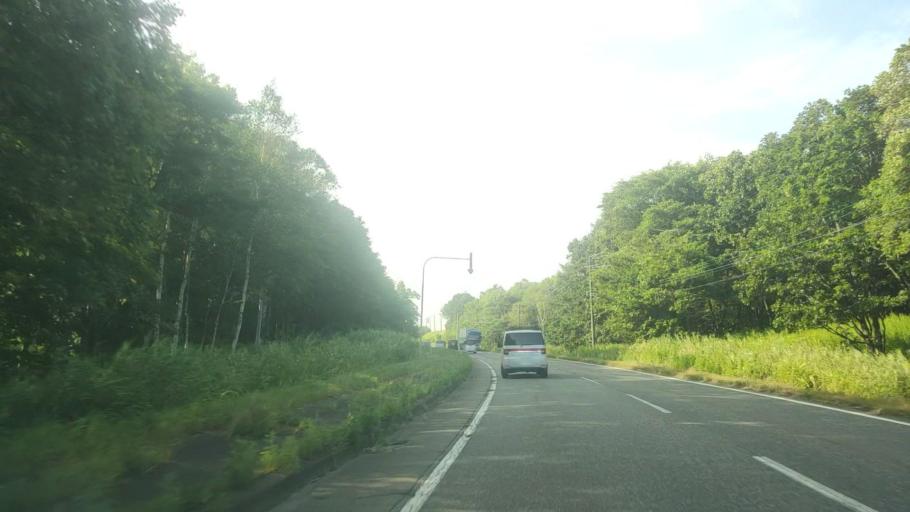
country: JP
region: Hokkaido
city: Chitose
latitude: 42.8058
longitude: 141.8343
